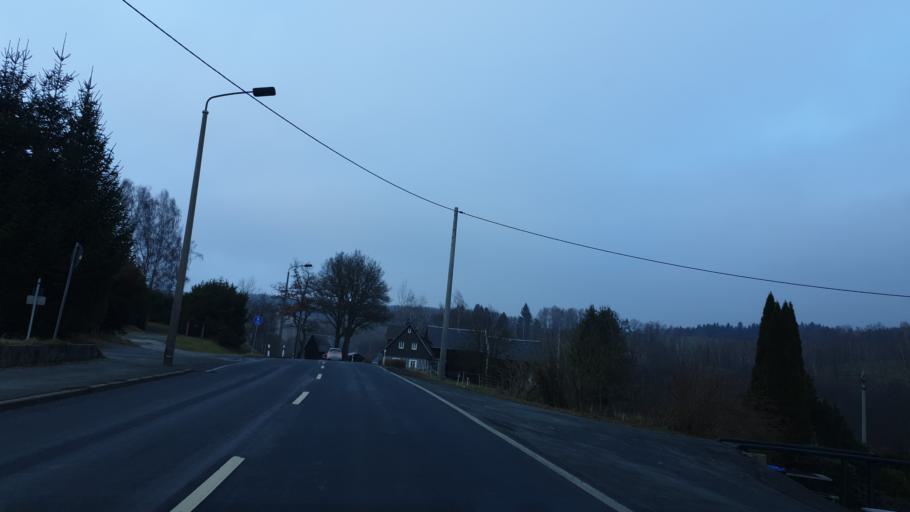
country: DE
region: Saxony
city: Adorf
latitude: 50.2885
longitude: 12.2729
